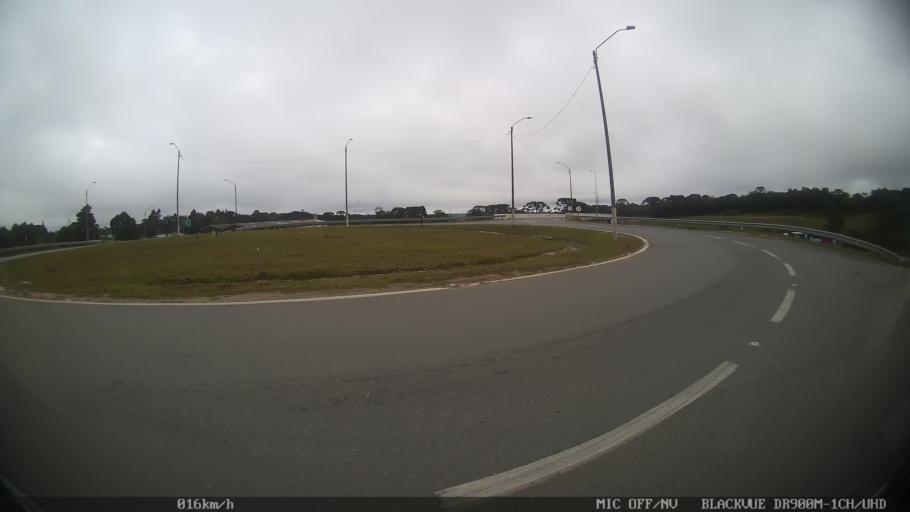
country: BR
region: Parana
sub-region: Sao Jose Dos Pinhais
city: Sao Jose dos Pinhais
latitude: -25.8210
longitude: -49.1270
